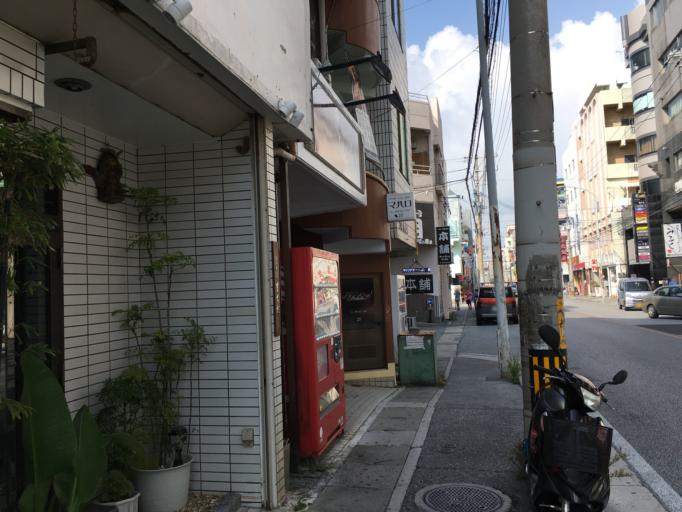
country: JP
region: Okinawa
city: Naha-shi
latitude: 26.2195
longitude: 127.6753
